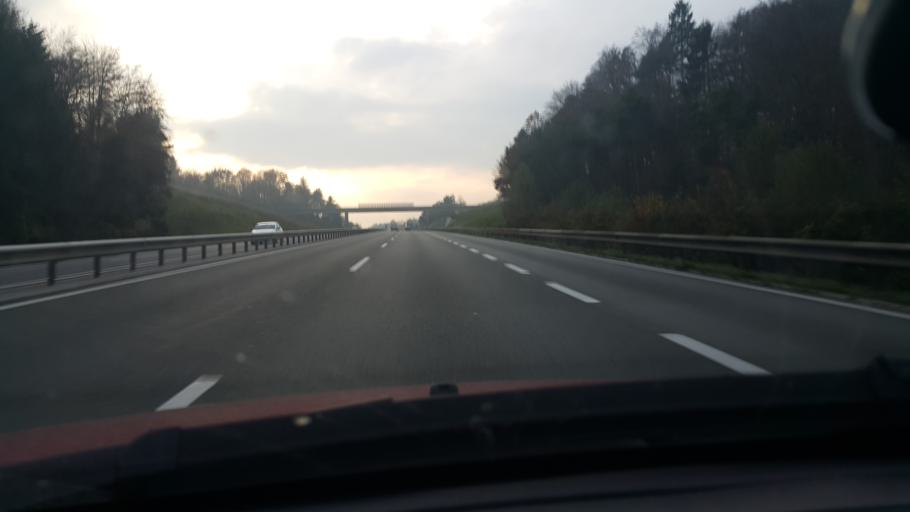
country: SI
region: Slovenska Bistrica
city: Slovenska Bistrica
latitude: 46.3699
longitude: 15.5282
